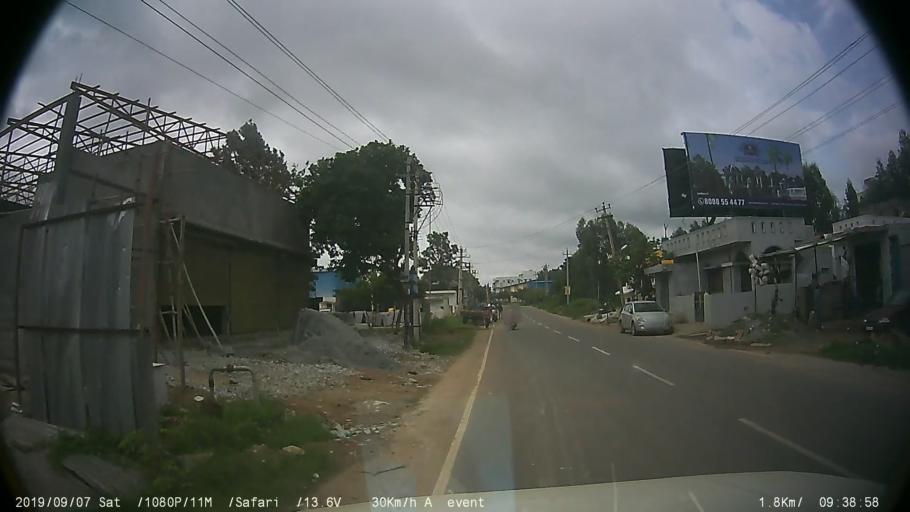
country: IN
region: Karnataka
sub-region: Bangalore Urban
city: Anekal
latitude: 12.8159
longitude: 77.6279
